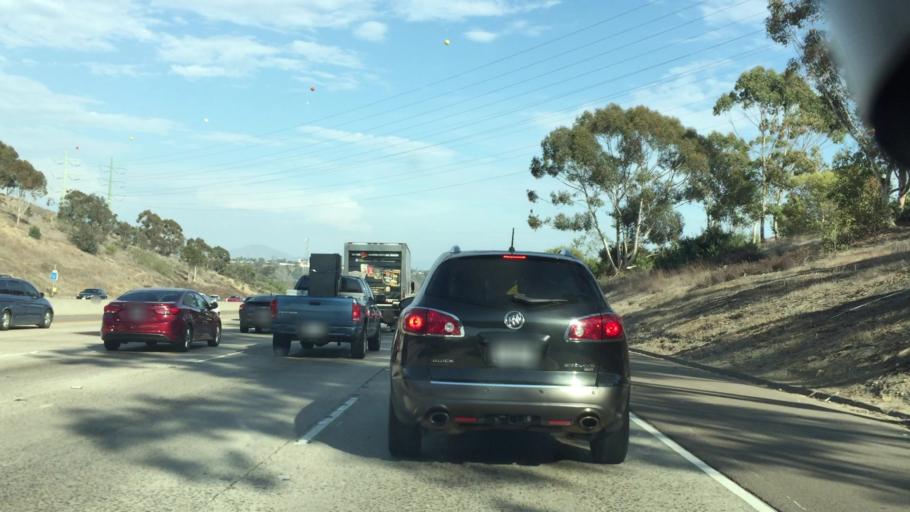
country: US
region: California
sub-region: San Diego County
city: San Diego
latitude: 32.7851
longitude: -117.1451
